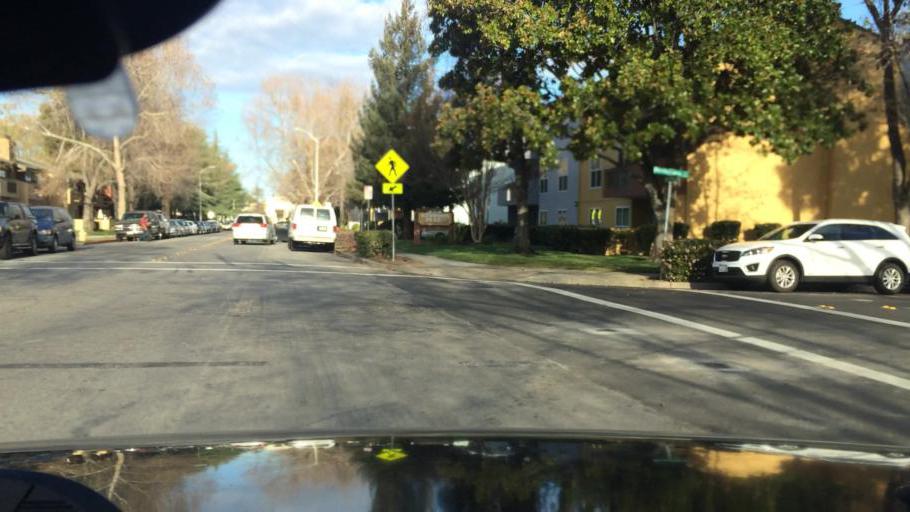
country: US
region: California
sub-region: Alameda County
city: Fremont
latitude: 37.5507
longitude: -121.9881
